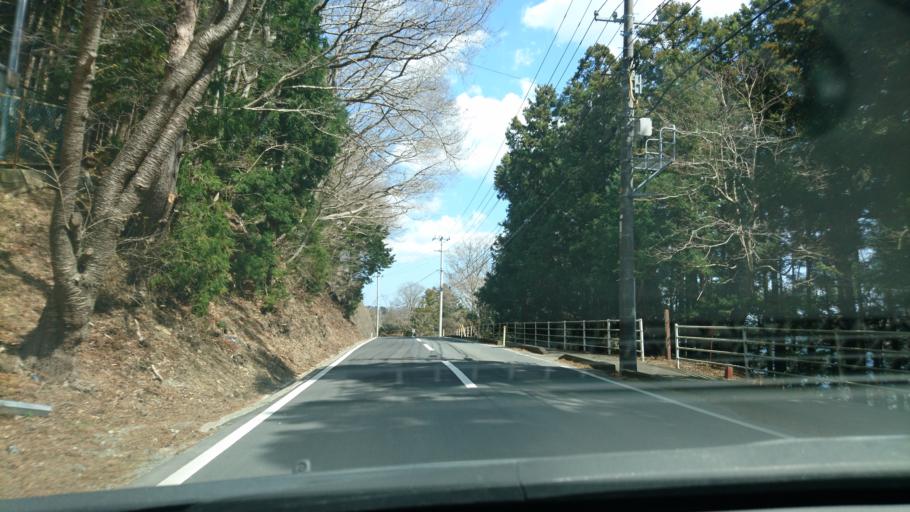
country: JP
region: Miyagi
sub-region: Oshika Gun
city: Onagawa Cho
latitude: 38.4690
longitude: 141.4778
